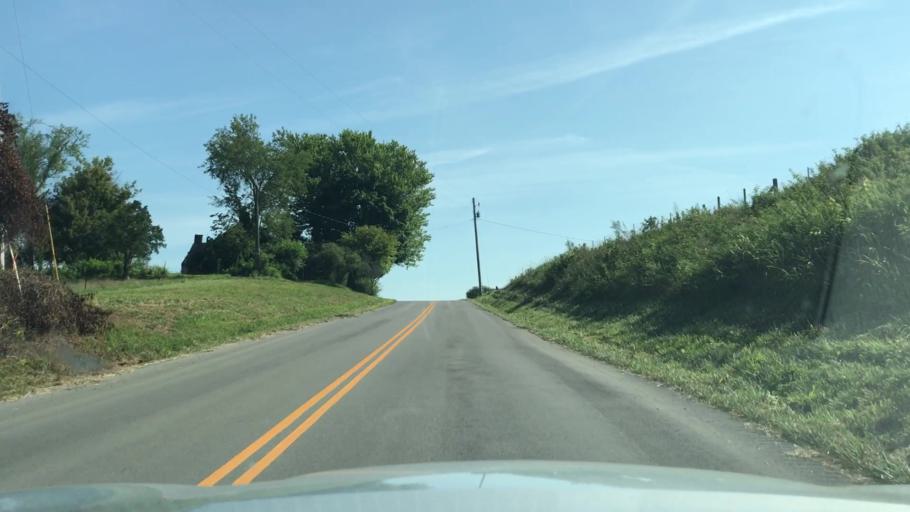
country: US
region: Kentucky
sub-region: Clinton County
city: Albany
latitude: 36.6642
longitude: -85.0733
